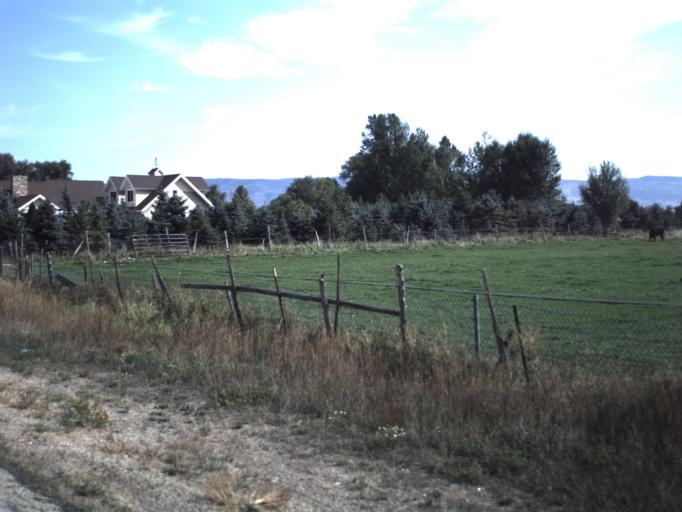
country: US
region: Utah
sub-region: Wasatch County
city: Midway
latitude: 40.4737
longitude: -111.4718
